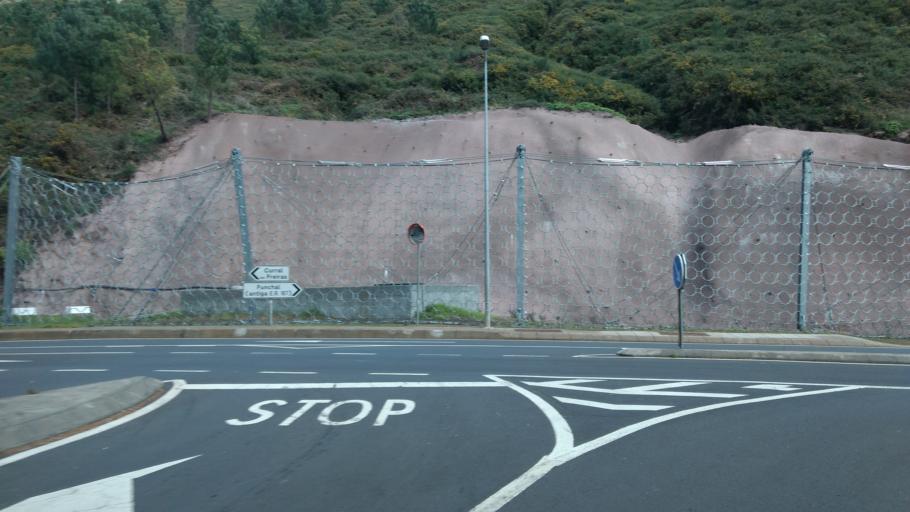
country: PT
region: Madeira
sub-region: Camara de Lobos
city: Curral das Freiras
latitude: 32.7051
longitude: -16.9549
